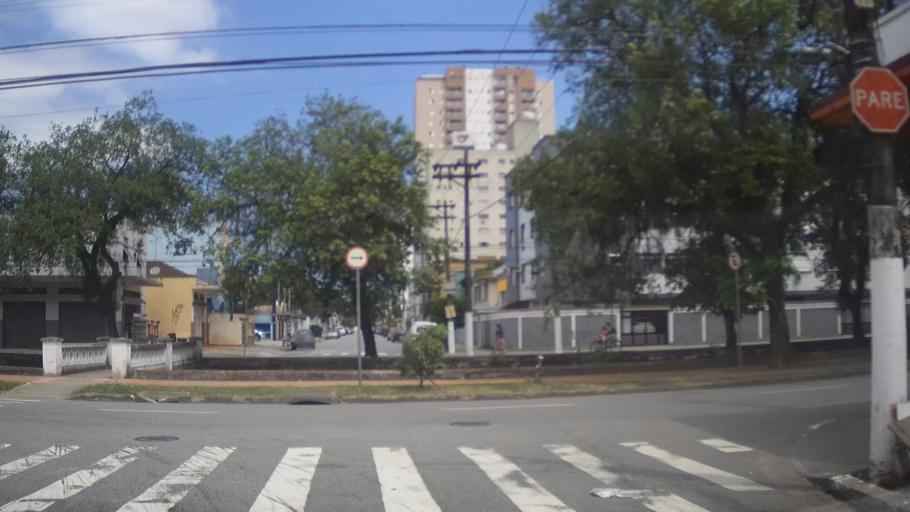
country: BR
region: Sao Paulo
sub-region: Santos
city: Santos
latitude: -23.9603
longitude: -46.3113
